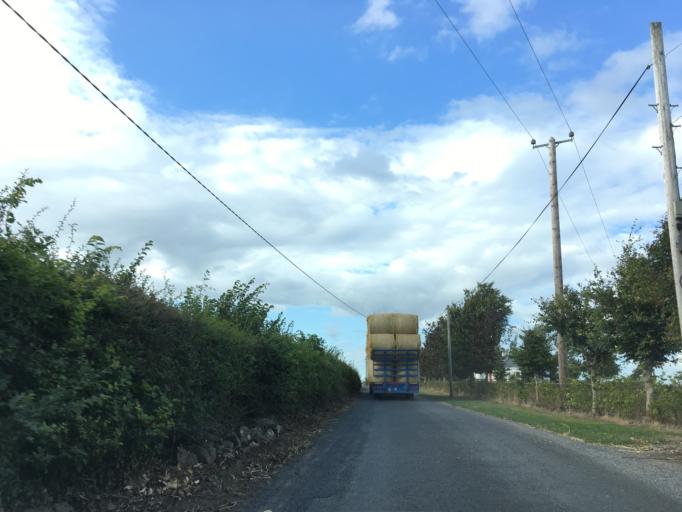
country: IE
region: Munster
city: Cahir
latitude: 52.3019
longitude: -7.9459
